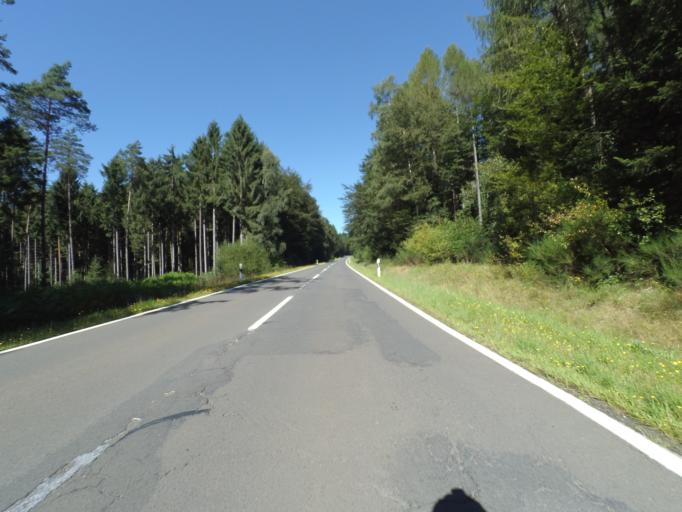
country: DE
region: Rheinland-Pfalz
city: Grosslittgen
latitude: 50.0360
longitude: 6.7701
